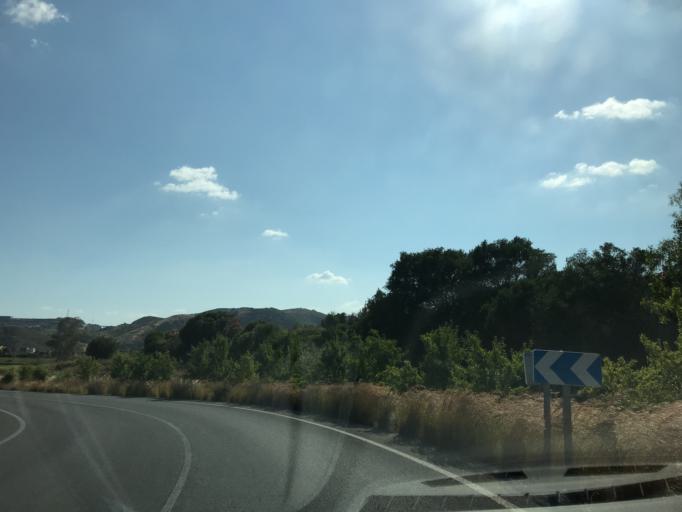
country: ES
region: Andalusia
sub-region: Provincia de Malaga
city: Benahavis
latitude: 36.5077
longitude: -5.0183
